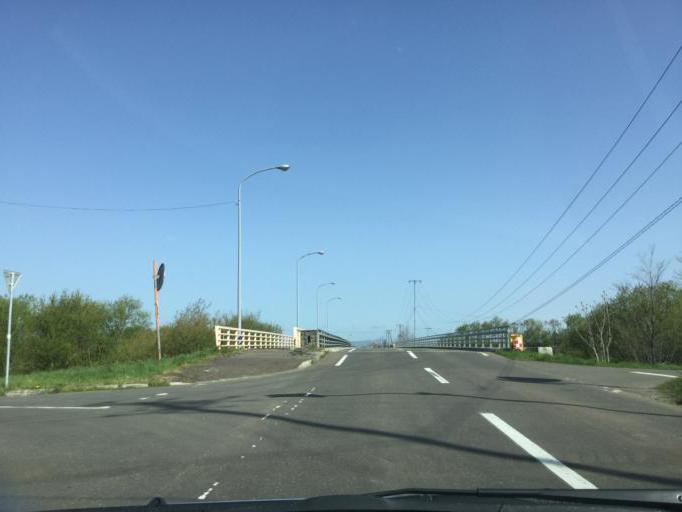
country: JP
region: Hokkaido
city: Iwamizawa
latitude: 43.1449
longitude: 141.7217
